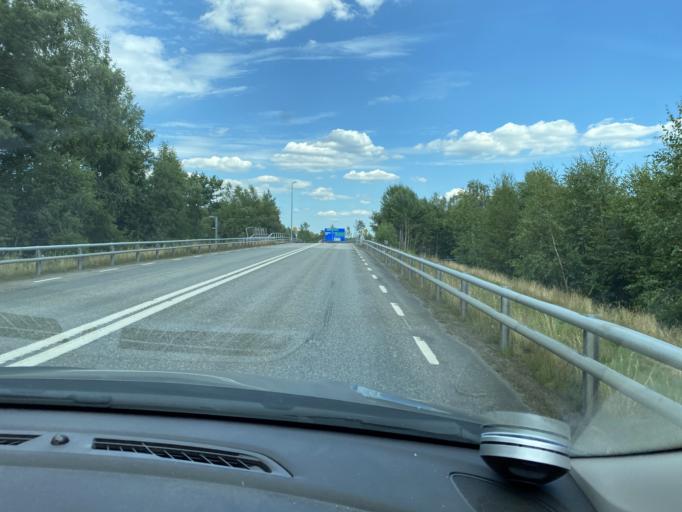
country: SE
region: Kronoberg
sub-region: Markaryds Kommun
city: Markaryd
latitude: 56.4470
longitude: 13.5966
